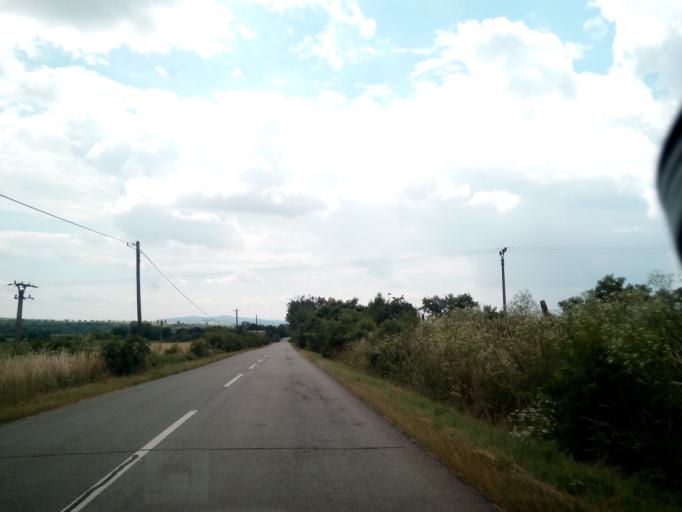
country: SK
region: Kosicky
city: Secovce
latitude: 48.5920
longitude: 21.5625
